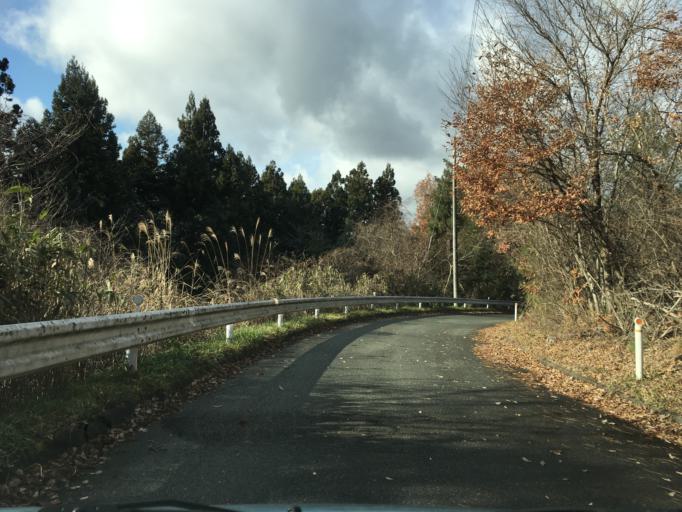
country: JP
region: Iwate
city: Ichinoseki
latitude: 38.8231
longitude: 141.2630
